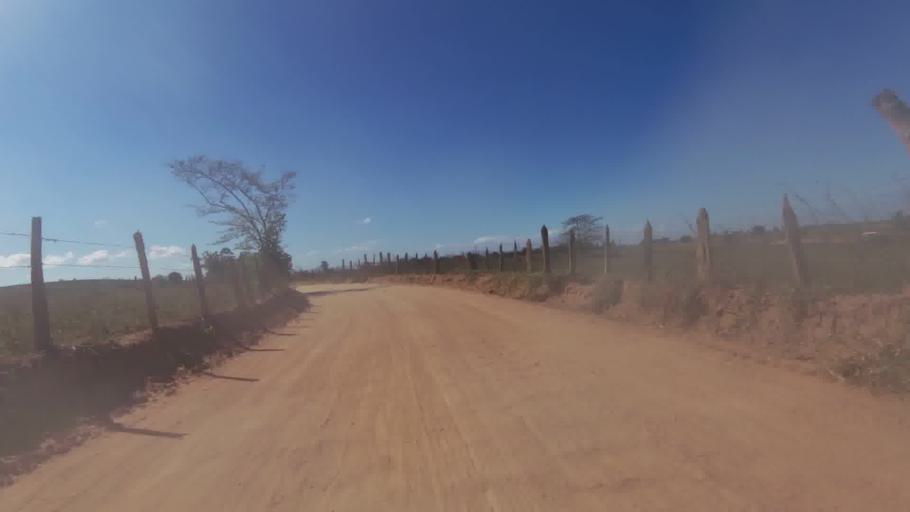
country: BR
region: Espirito Santo
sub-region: Marataizes
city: Marataizes
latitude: -21.1402
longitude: -40.9913
